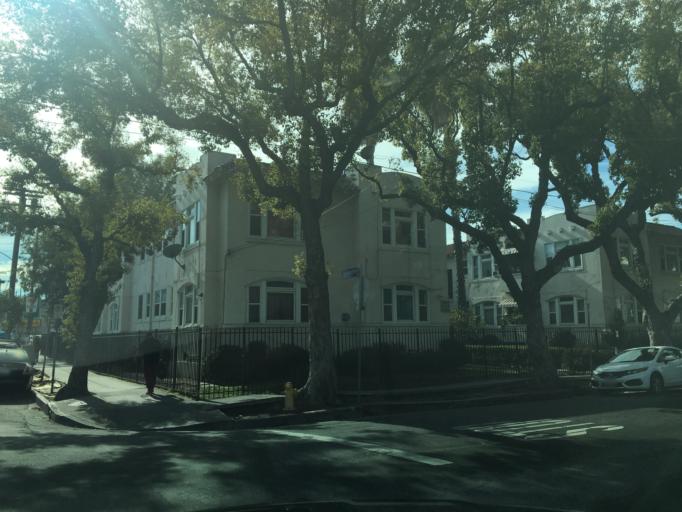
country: US
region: California
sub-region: Los Angeles County
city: Silver Lake
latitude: 34.0568
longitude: -118.2891
